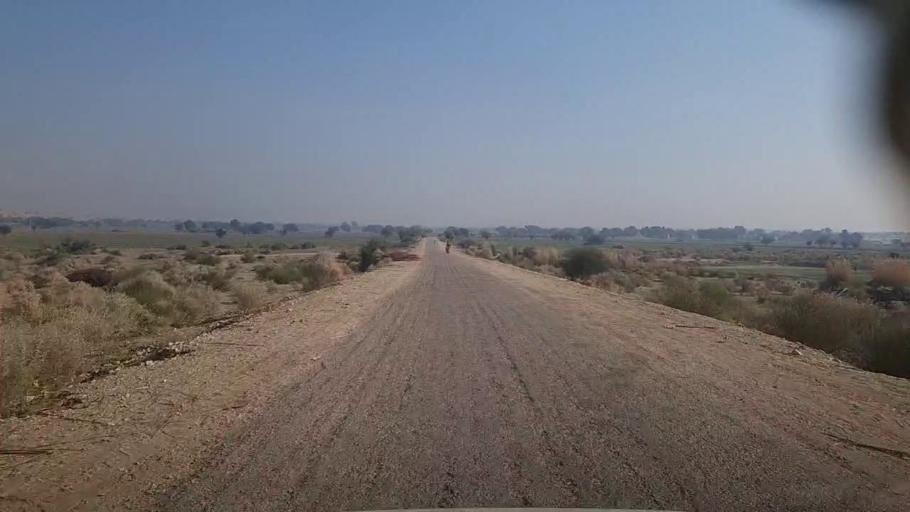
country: PK
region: Sindh
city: Kandiari
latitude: 26.8218
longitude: 68.4908
